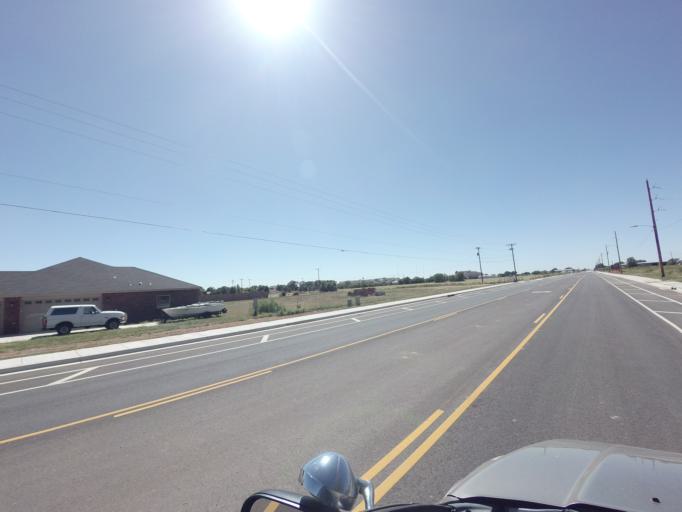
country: US
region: New Mexico
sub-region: Curry County
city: Clovis
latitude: 34.4483
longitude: -103.1916
